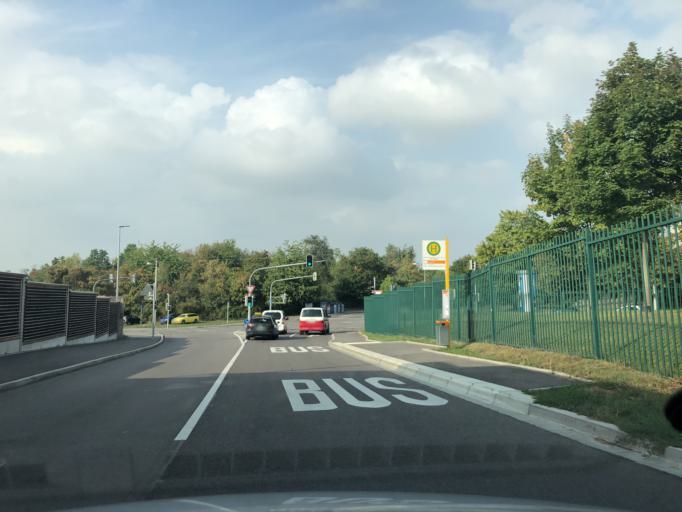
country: DE
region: Baden-Wuerttemberg
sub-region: Regierungsbezirk Stuttgart
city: Kornwestheim
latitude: 48.8271
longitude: 9.1914
